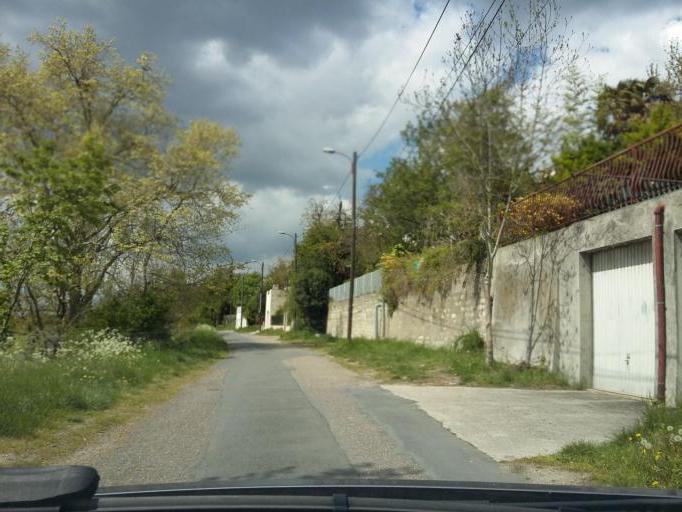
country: FR
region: Ile-de-France
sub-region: Departement de Seine-Saint-Denis
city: Epinay-sur-Seine
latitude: 48.9525
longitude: 2.3016
